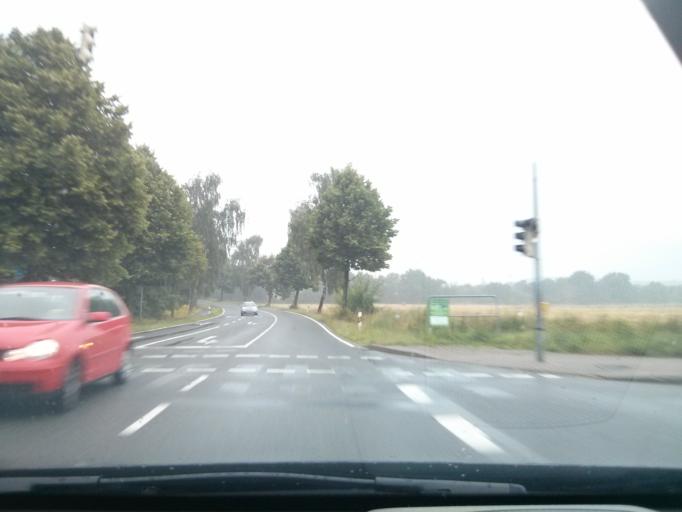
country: DE
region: Lower Saxony
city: Bendestorf
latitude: 53.3661
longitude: 9.9328
